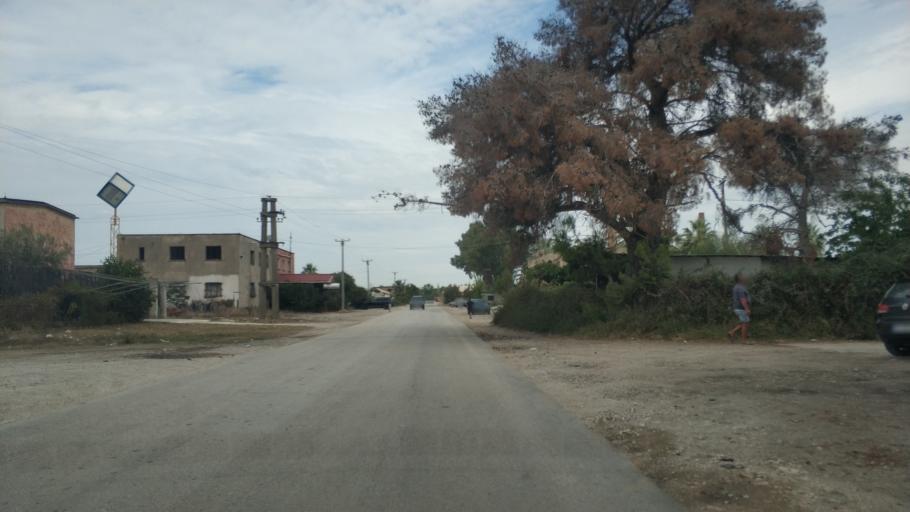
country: AL
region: Vlore
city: Vlore
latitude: 40.4724
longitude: 19.4573
